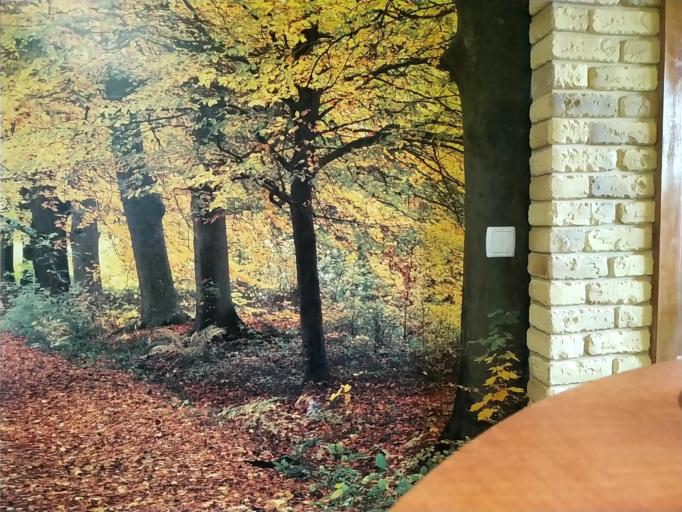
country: RU
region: Novgorod
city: Opechenskiy Posad
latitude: 58.2670
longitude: 34.0269
